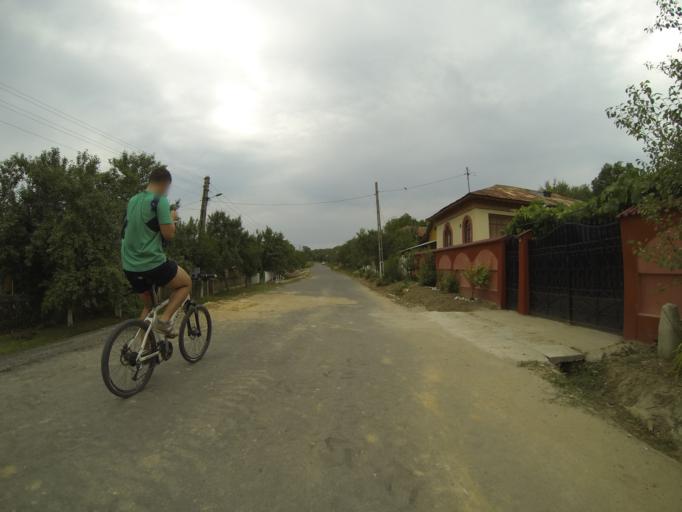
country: RO
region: Dolj
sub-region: Comuna Cotofenii din Fata
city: Cotofenii din Fata
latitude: 44.4922
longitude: 23.6702
